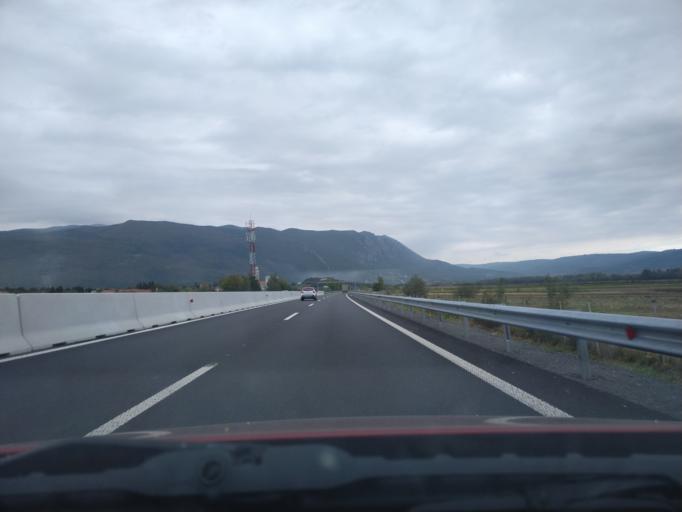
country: SI
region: Ajdovscina
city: Ajdovscina
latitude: 45.8688
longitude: 13.9296
